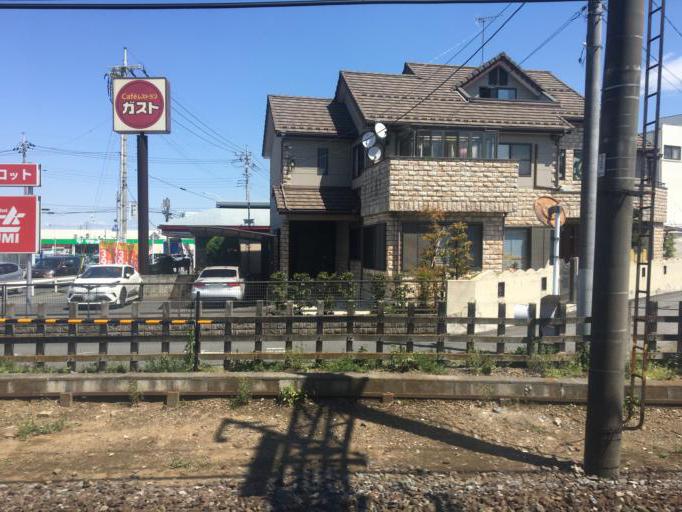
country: JP
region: Saitama
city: Kawagoe
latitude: 35.9258
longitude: 139.4423
